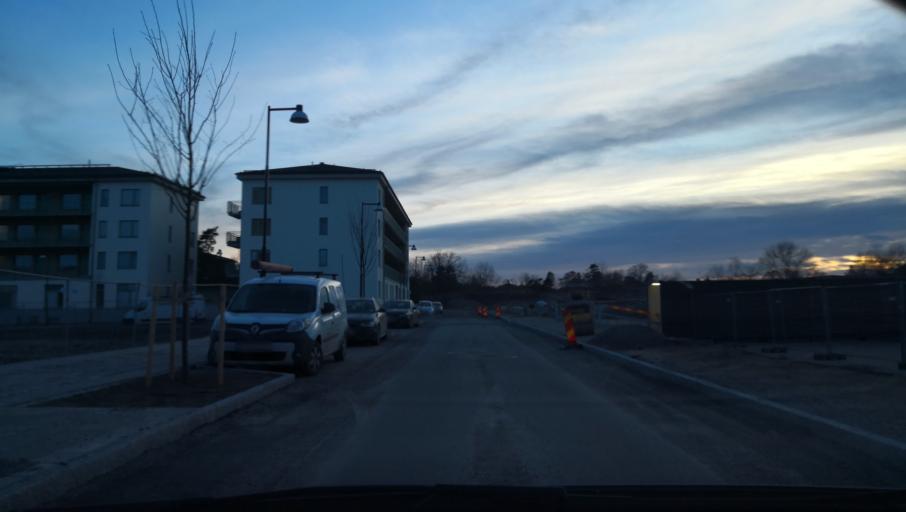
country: SE
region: Stockholm
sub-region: Varmdo Kommun
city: Gustavsberg
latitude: 59.3212
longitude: 18.3825
